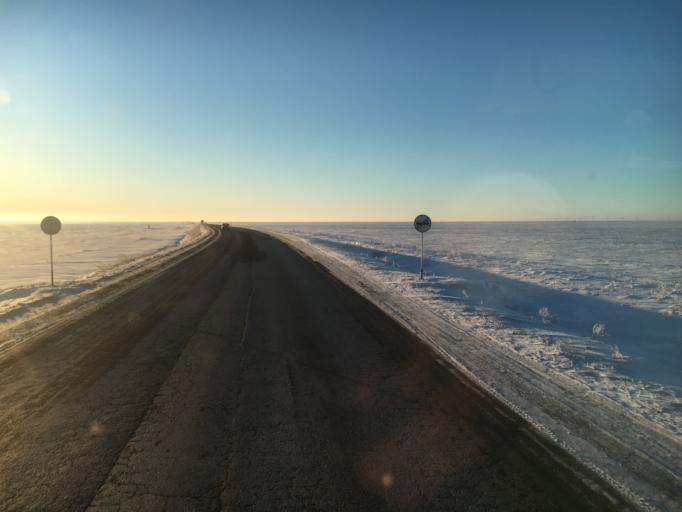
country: KZ
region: Aqtoebe
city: Khromtau
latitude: 50.2517
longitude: 58.3635
